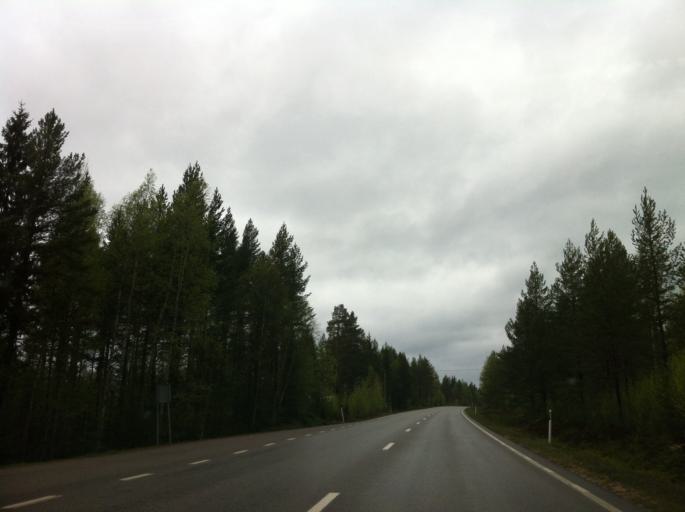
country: SE
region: Jaemtland
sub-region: Harjedalens Kommun
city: Sveg
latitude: 62.0472
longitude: 14.3308
